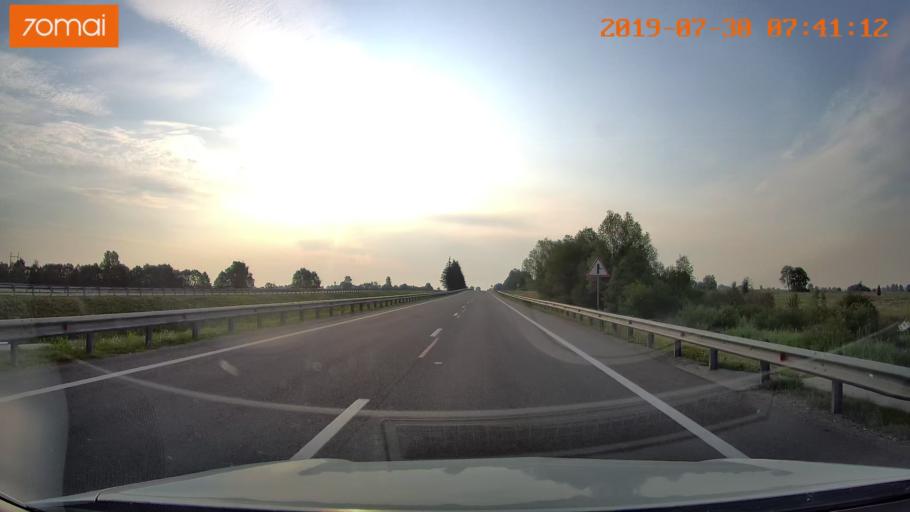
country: RU
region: Kaliningrad
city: Gvardeysk
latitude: 54.6483
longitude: 21.2452
